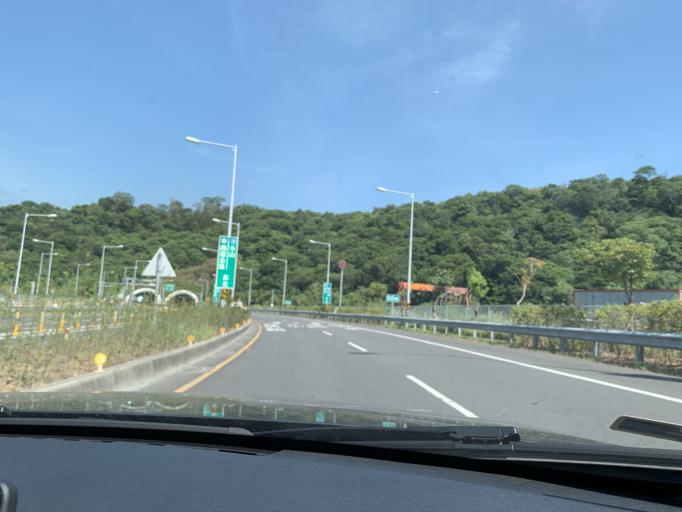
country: TW
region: Taiwan
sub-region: Yilan
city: Yilan
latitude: 24.5907
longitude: 121.8489
